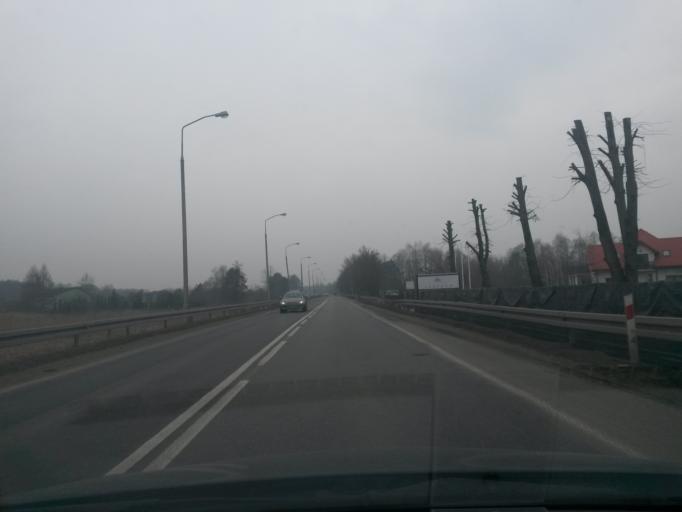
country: PL
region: Masovian Voivodeship
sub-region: Powiat legionowski
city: Nieporet
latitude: 52.4405
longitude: 21.0162
